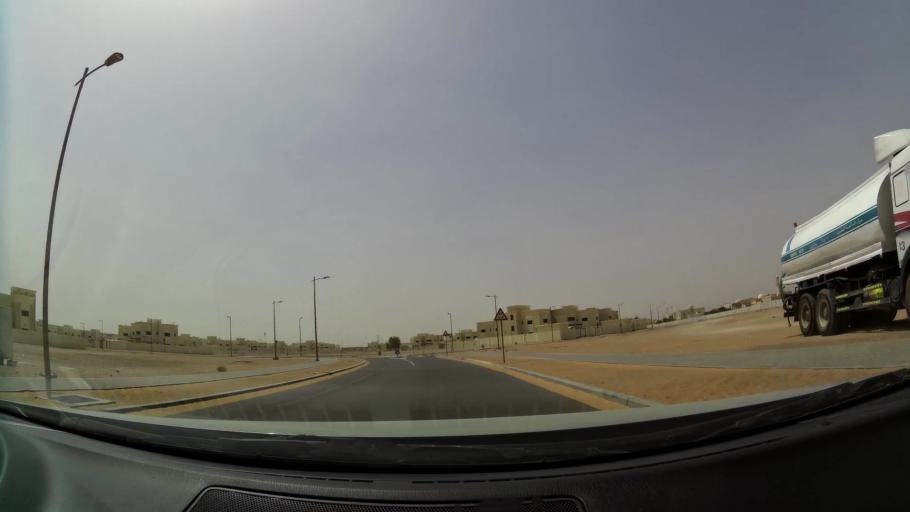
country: AE
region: Abu Dhabi
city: Al Ain
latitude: 24.1373
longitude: 55.6320
